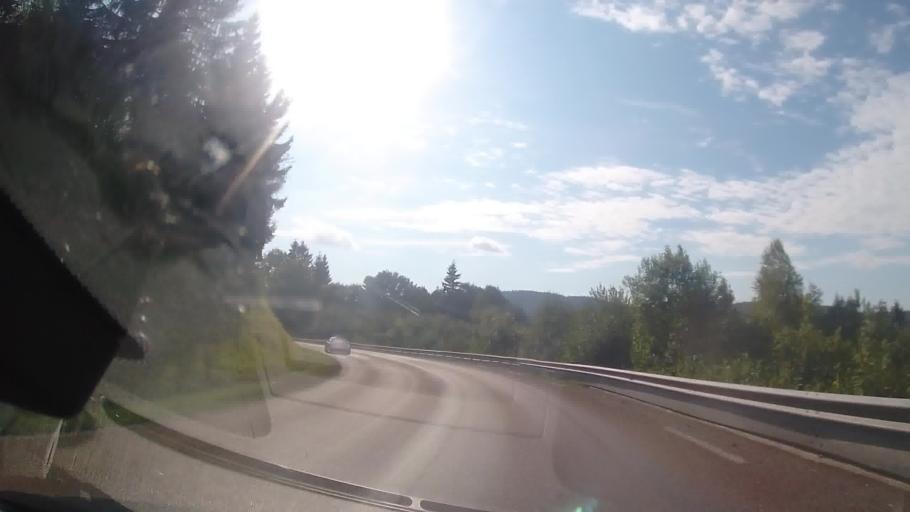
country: FR
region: Franche-Comte
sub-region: Departement du Jura
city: Morbier
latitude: 46.5999
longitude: 5.9139
